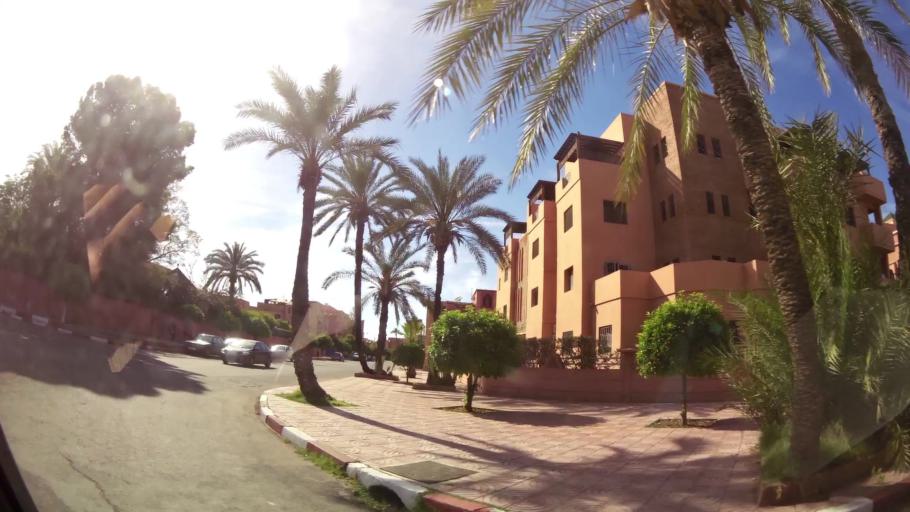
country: MA
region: Marrakech-Tensift-Al Haouz
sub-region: Marrakech
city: Marrakesh
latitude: 31.6514
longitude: -8.0111
